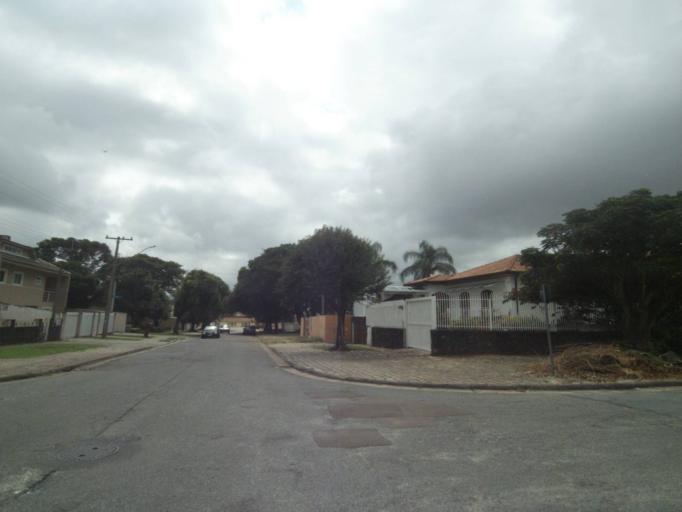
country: BR
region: Parana
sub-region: Pinhais
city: Pinhais
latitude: -25.4511
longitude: -49.2167
